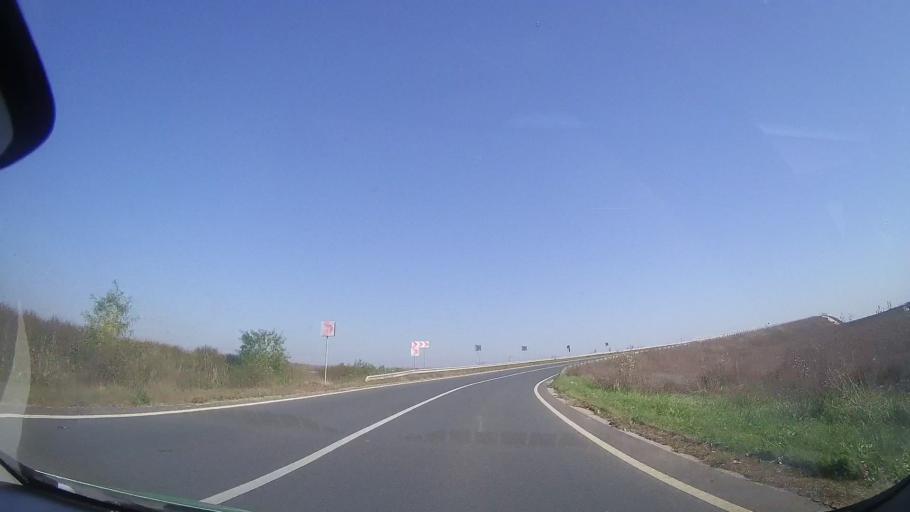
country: RO
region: Timis
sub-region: Comuna Balint
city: Balint
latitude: 45.7873
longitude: 21.8492
